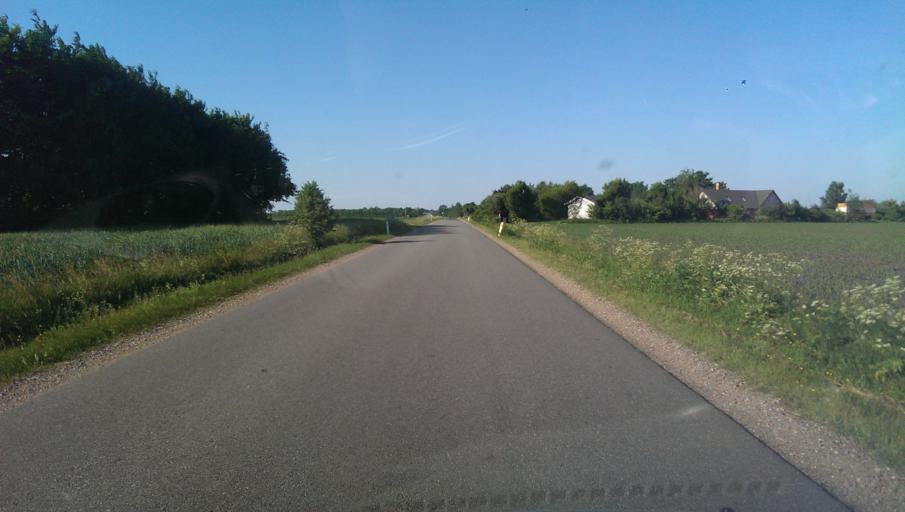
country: DK
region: South Denmark
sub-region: Esbjerg Kommune
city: Bramming
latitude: 55.5368
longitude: 8.6958
